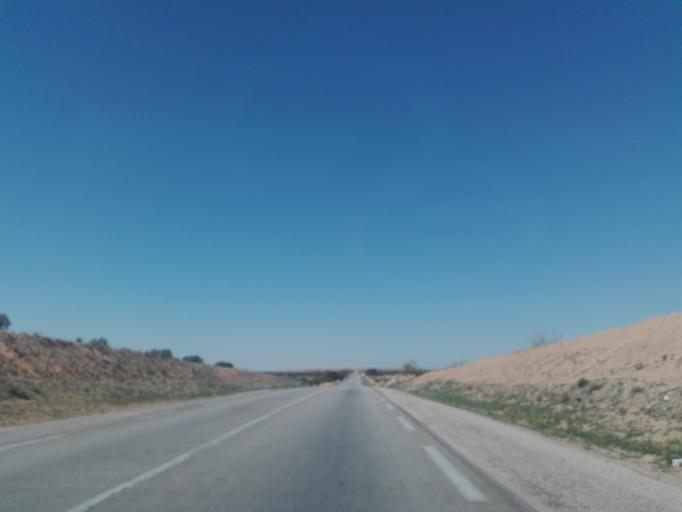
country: TN
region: Safaqis
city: Bi'r `Ali Bin Khalifah
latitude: 34.7577
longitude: 10.2789
